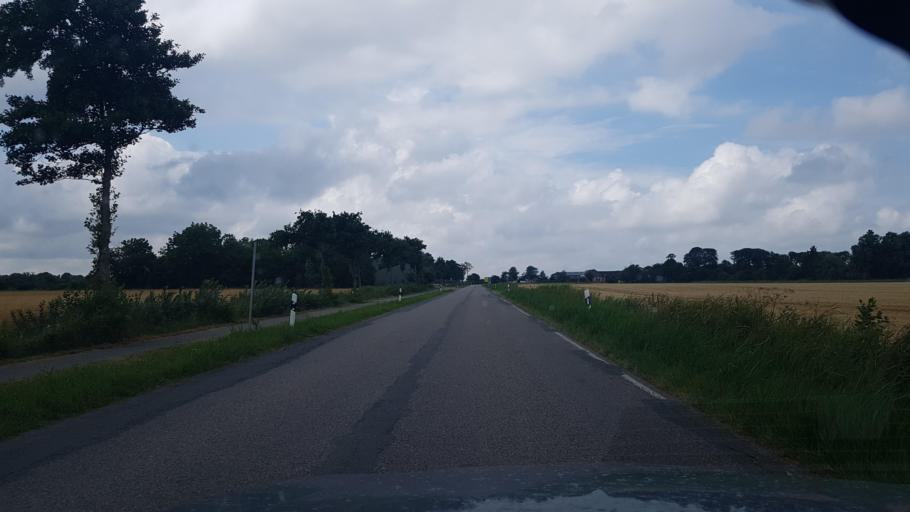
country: DE
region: Schleswig-Holstein
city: Elisabeth-Sophien-Koog
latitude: 54.4905
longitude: 8.8554
